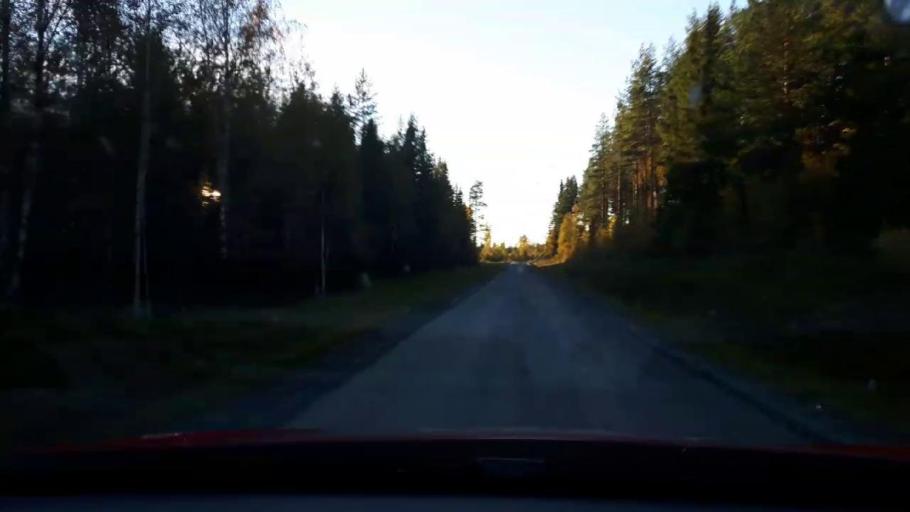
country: SE
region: Jaemtland
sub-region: Krokoms Kommun
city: Krokom
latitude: 63.4220
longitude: 14.4849
